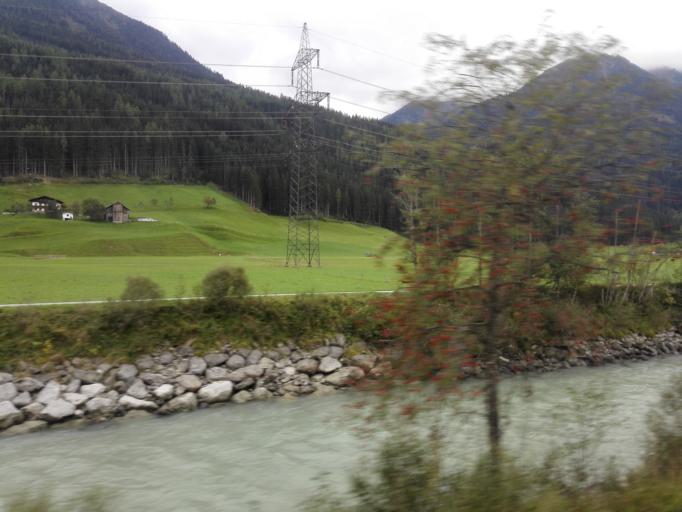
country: AT
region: Salzburg
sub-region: Politischer Bezirk Zell am See
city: Bramberg am Wildkogel
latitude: 47.2590
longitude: 12.3273
